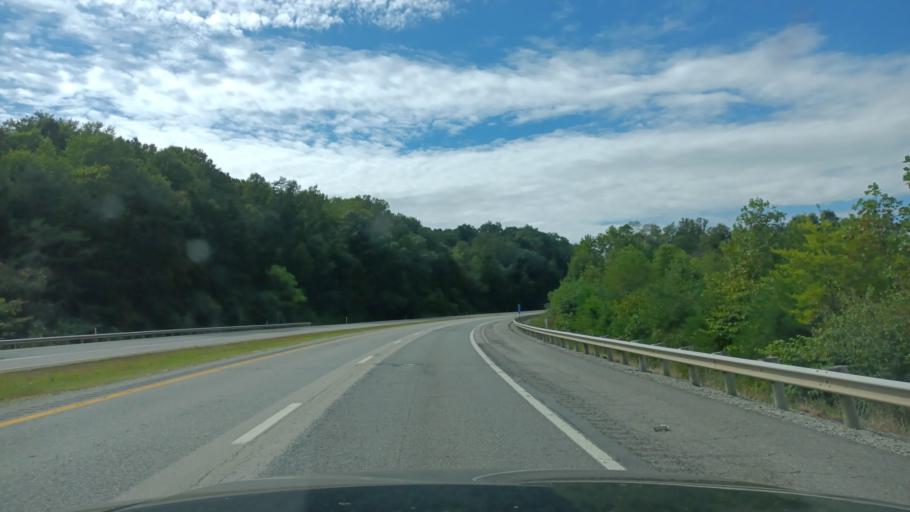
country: US
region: West Virginia
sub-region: Doddridge County
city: West Union
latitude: 39.2743
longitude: -80.8546
